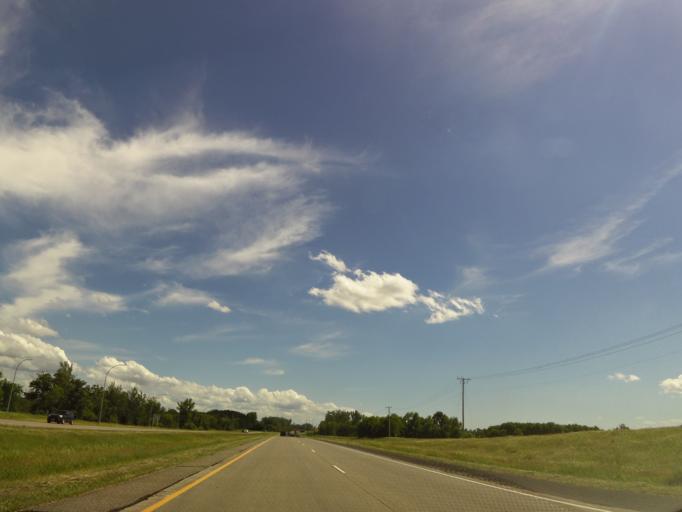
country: US
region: Minnesota
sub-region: Stearns County
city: Sartell
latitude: 45.6525
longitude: -94.1774
